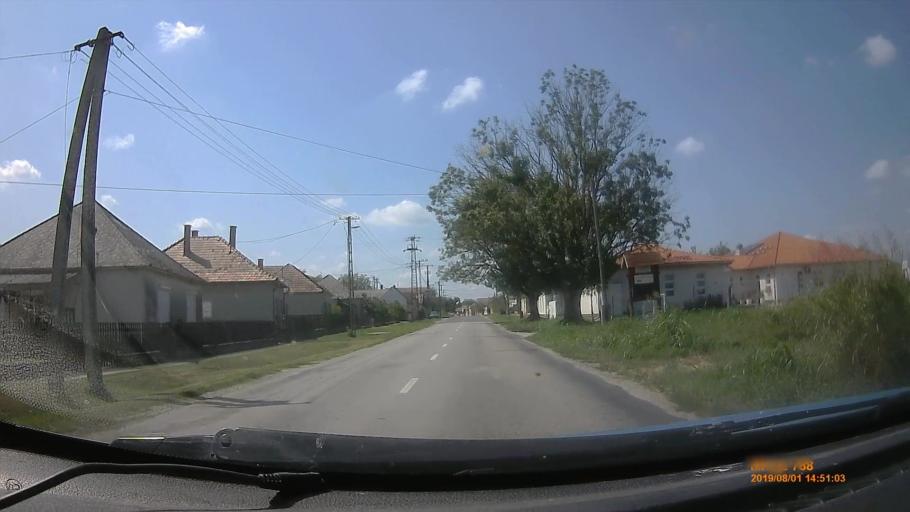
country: HU
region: Baranya
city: Vajszlo
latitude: 45.8542
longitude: 17.9980
